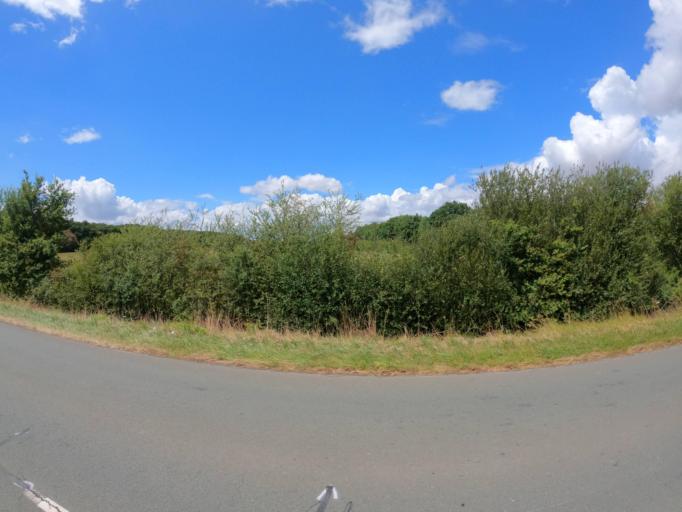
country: FR
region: Pays de la Loire
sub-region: Departement de Maine-et-Loire
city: Champigne
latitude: 47.6904
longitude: -0.5509
